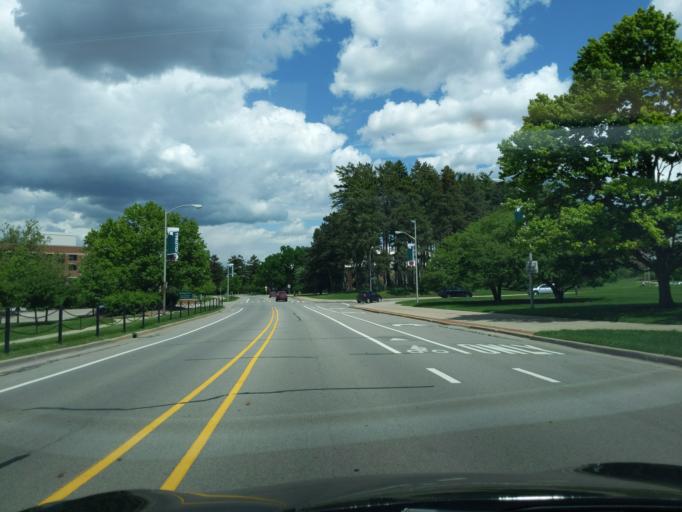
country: US
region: Michigan
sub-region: Ingham County
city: East Lansing
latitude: 42.7294
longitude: -84.4918
